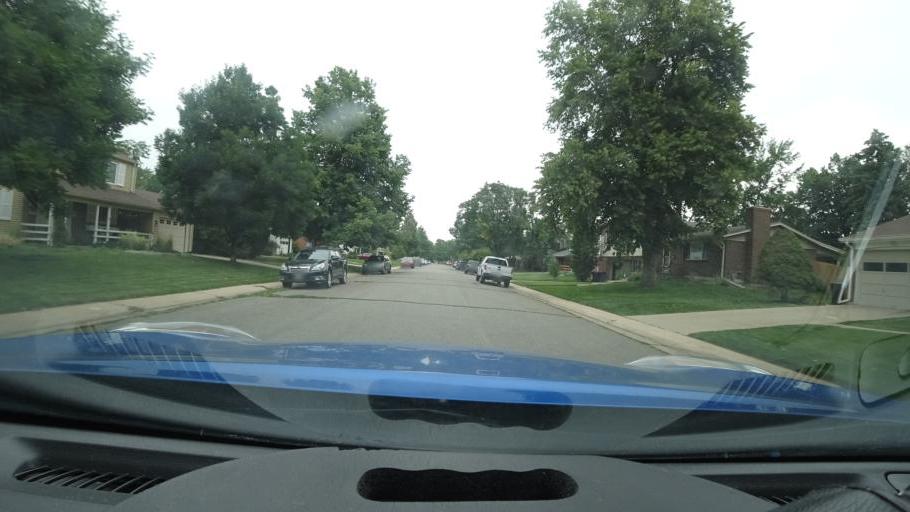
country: US
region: Colorado
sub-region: Arapahoe County
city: Glendale
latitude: 39.6805
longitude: -104.9160
